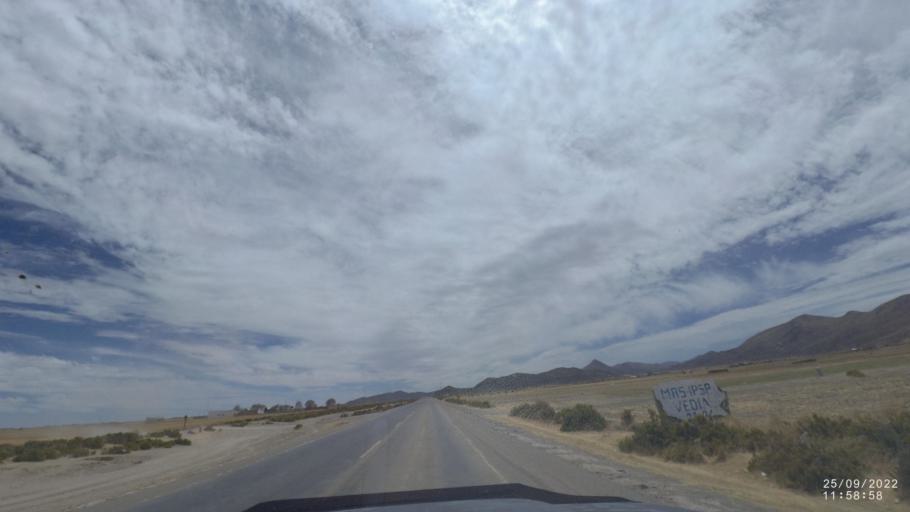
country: BO
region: Oruro
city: Challapata
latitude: -18.7953
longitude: -66.8426
